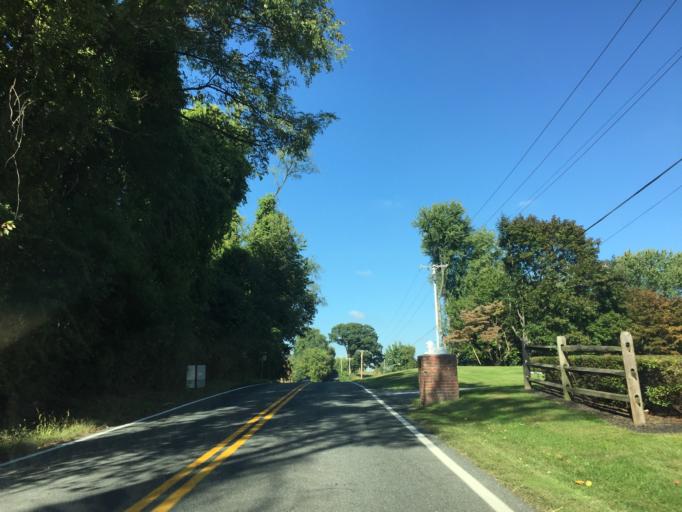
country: US
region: Maryland
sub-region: Harford County
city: Bel Air North
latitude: 39.5733
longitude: -76.4240
